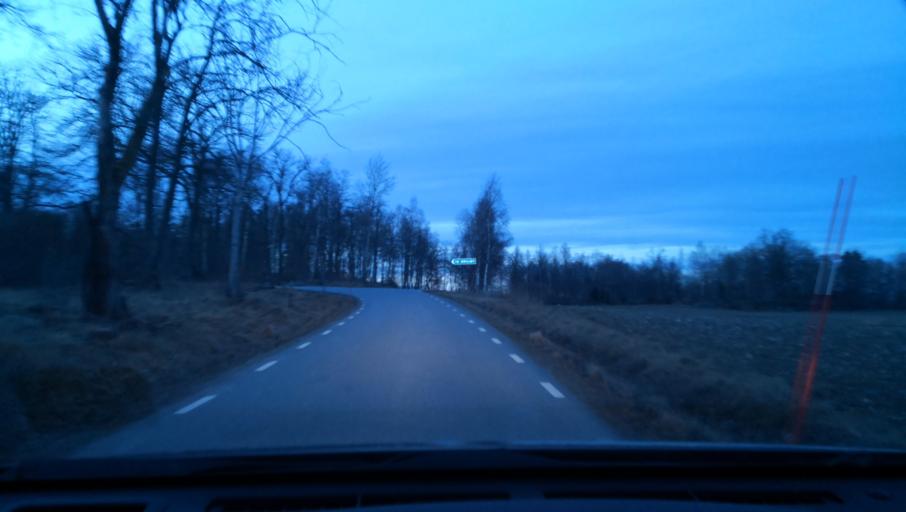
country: SE
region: Uppsala
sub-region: Enkopings Kommun
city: Dalby
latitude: 59.5495
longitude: 17.3688
